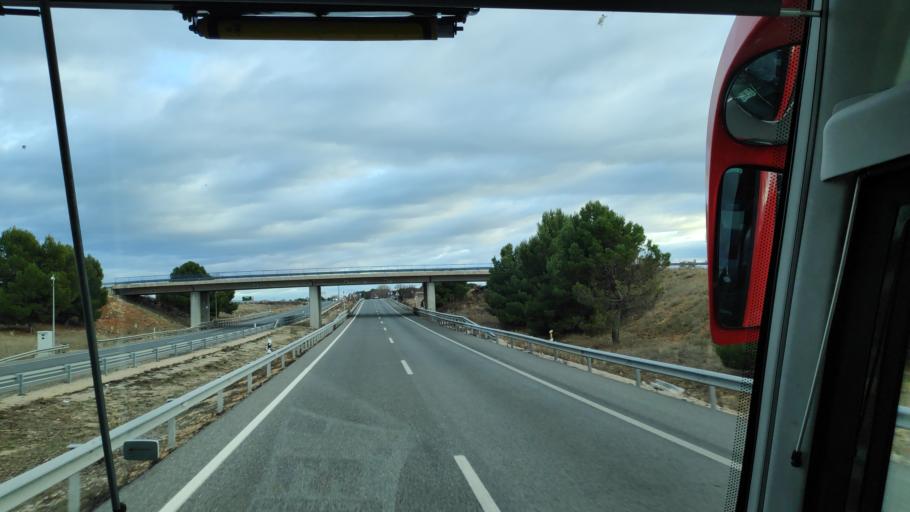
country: ES
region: Madrid
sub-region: Provincia de Madrid
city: Villarejo de Salvanes
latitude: 40.1723
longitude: -3.2931
